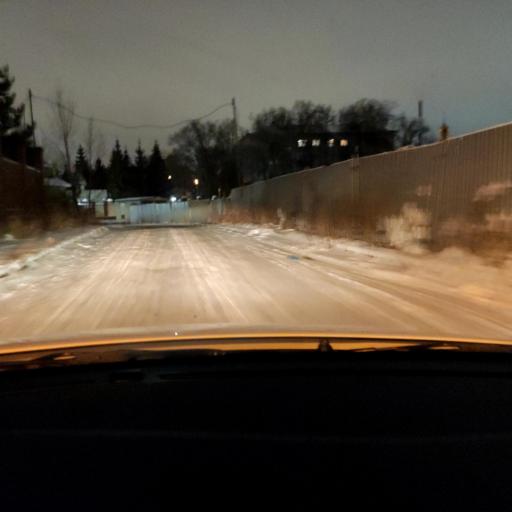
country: RU
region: Tatarstan
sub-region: Gorod Kazan'
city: Kazan
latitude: 55.7957
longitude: 49.1454
